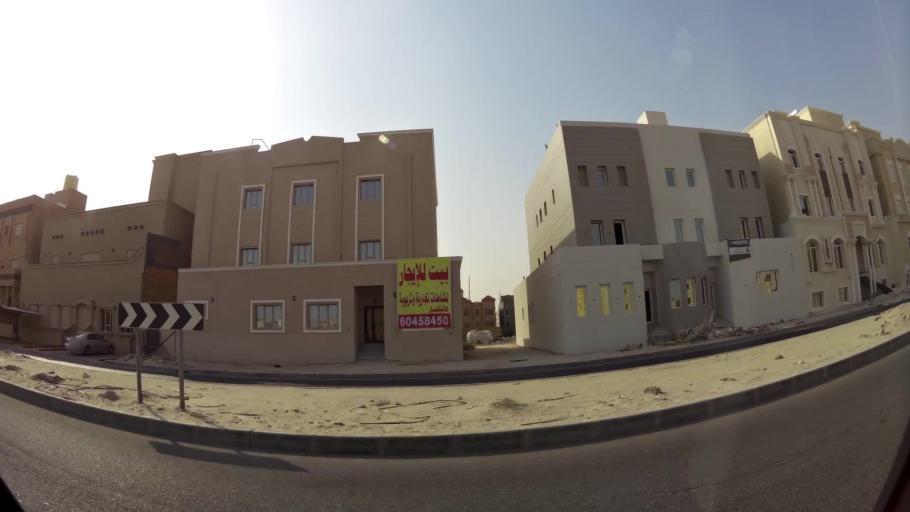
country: KW
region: Al Asimah
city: Ar Rabiyah
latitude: 29.3279
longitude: 47.8046
